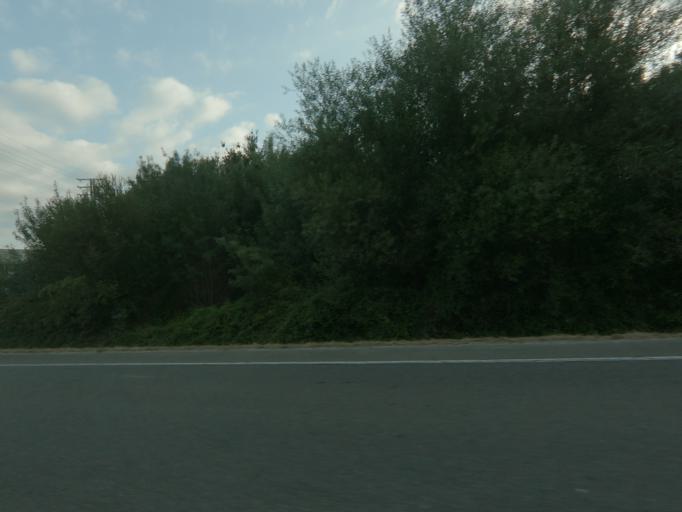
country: ES
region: Galicia
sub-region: Provincia de Ourense
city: Taboadela
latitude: 42.2796
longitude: -7.8372
